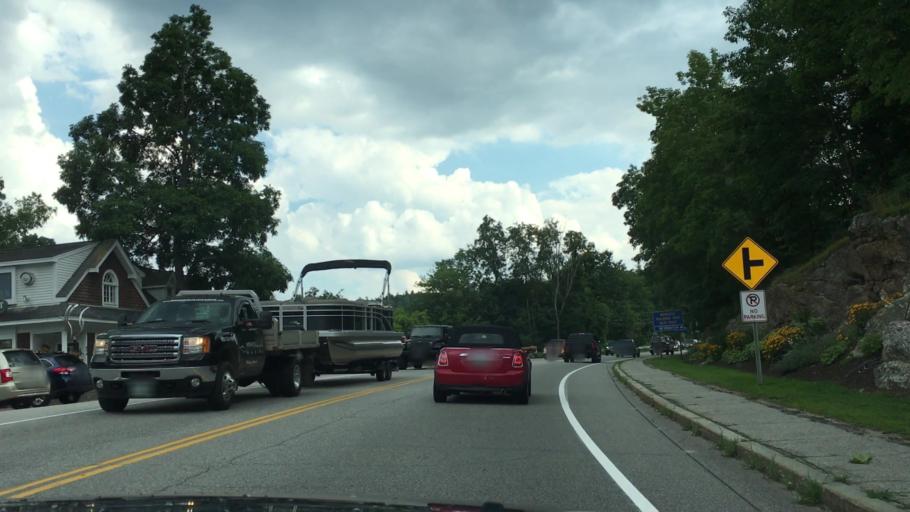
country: US
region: New Hampshire
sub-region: Belknap County
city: Meredith
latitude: 43.6537
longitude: -71.4969
